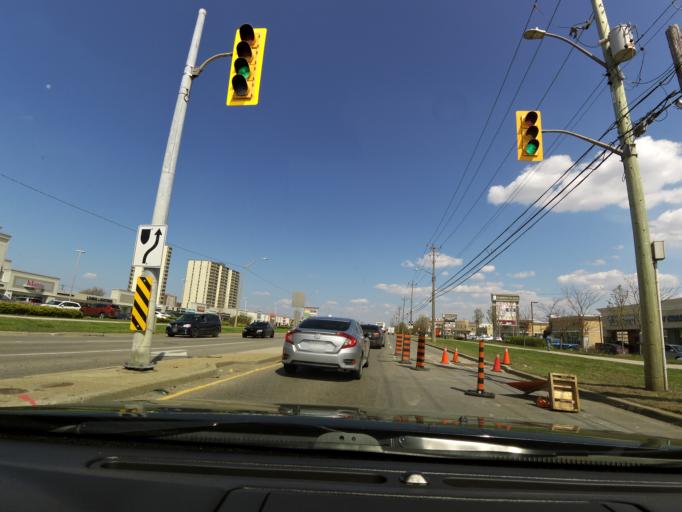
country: CA
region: Ontario
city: Kitchener
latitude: 43.4200
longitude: -80.4483
